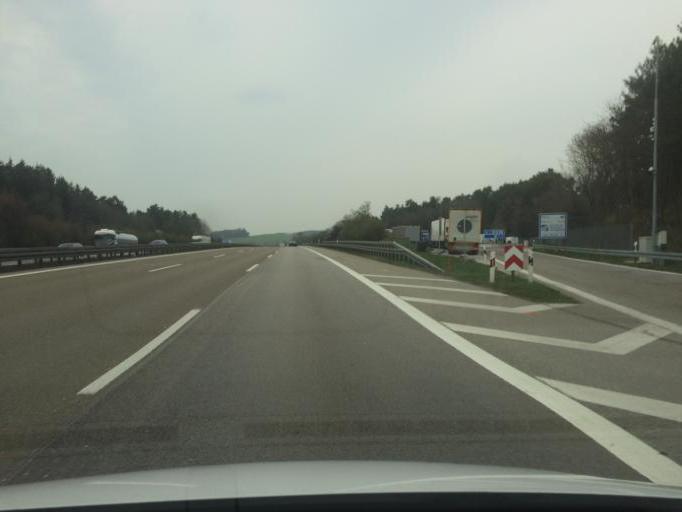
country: DE
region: Bavaria
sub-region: Upper Bavaria
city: Rohrbach
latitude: 48.6099
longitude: 11.5439
